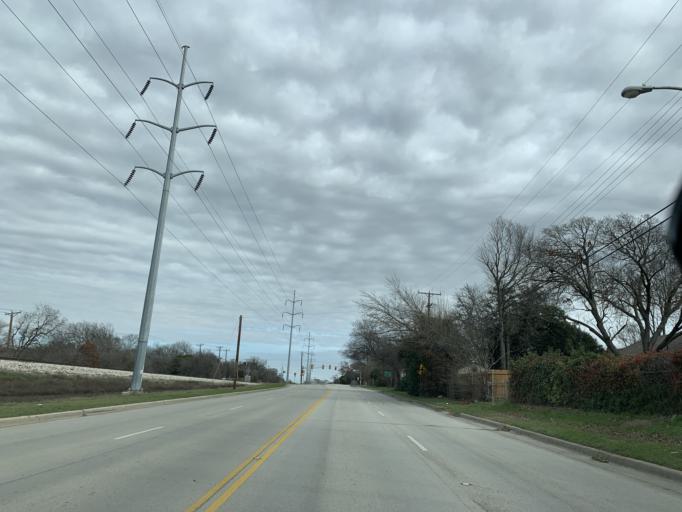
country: US
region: Texas
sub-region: Tarrant County
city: Edgecliff Village
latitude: 32.6770
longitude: -97.3784
